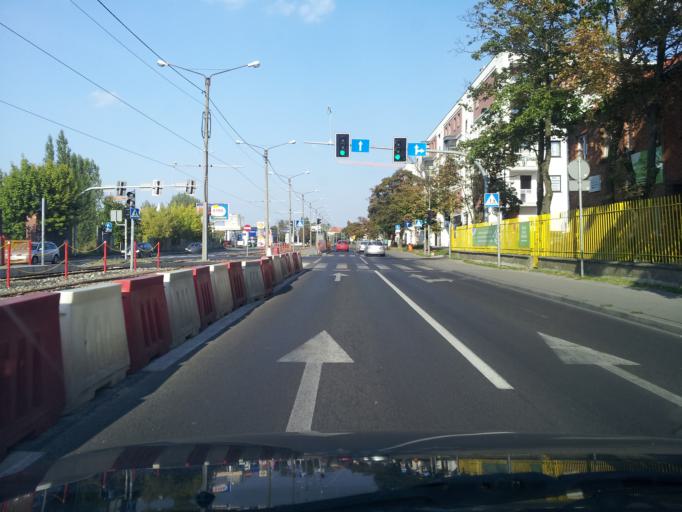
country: PL
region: Kujawsko-Pomorskie
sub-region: Torun
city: Torun
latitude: 53.0179
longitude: 18.6385
